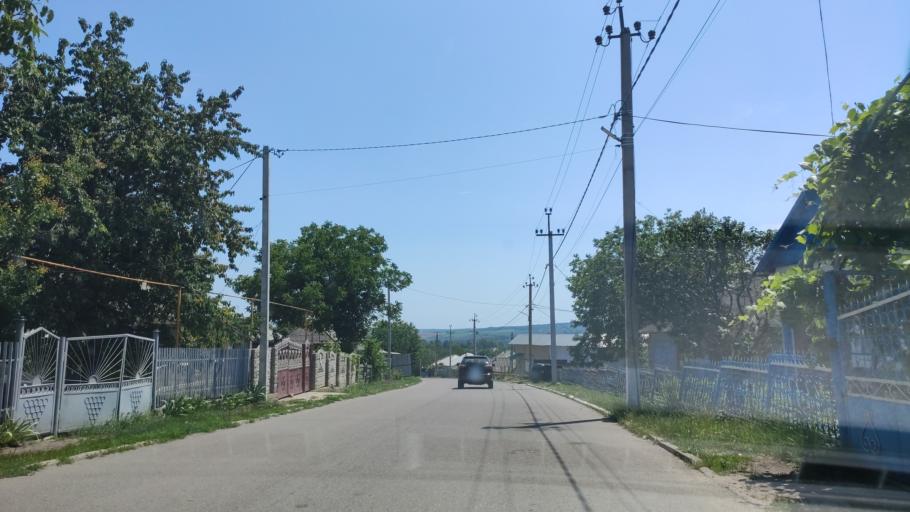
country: MD
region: Raionul Soroca
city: Soroca
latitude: 48.1495
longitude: 28.2793
